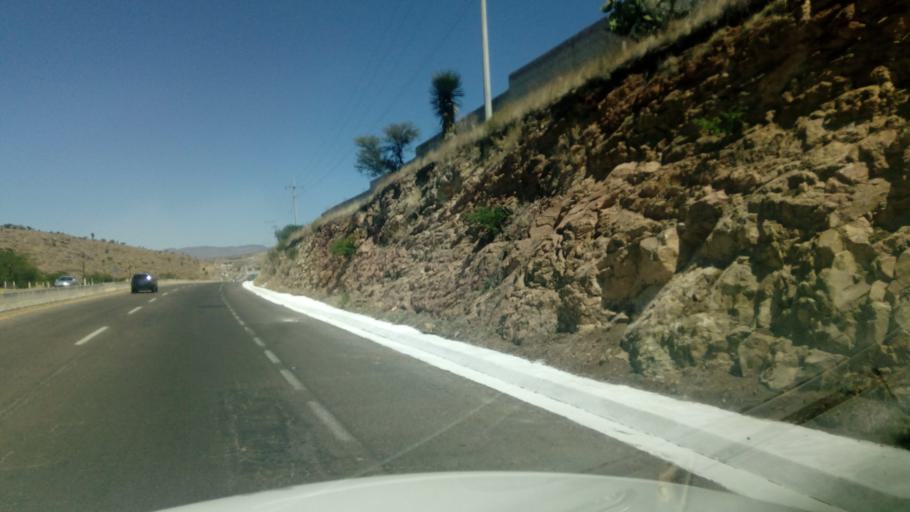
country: MX
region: Durango
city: Victoria de Durango
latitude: 24.0893
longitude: -104.6810
